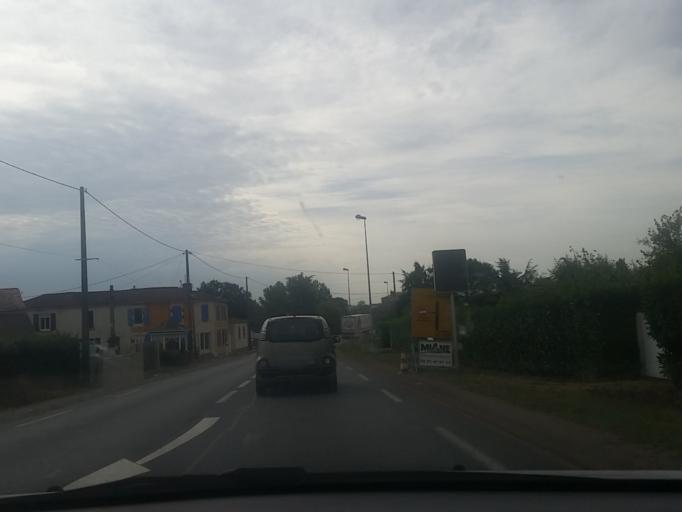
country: FR
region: Pays de la Loire
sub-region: Departement de la Vendee
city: Saint-Fulgent
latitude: 46.8324
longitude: -1.1574
